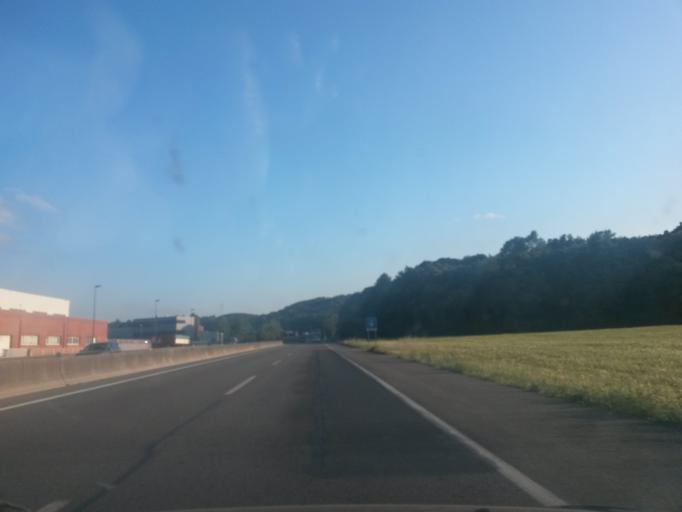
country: ES
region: Catalonia
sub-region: Provincia de Girona
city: Palol de Revardit
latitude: 42.0690
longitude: 2.8139
